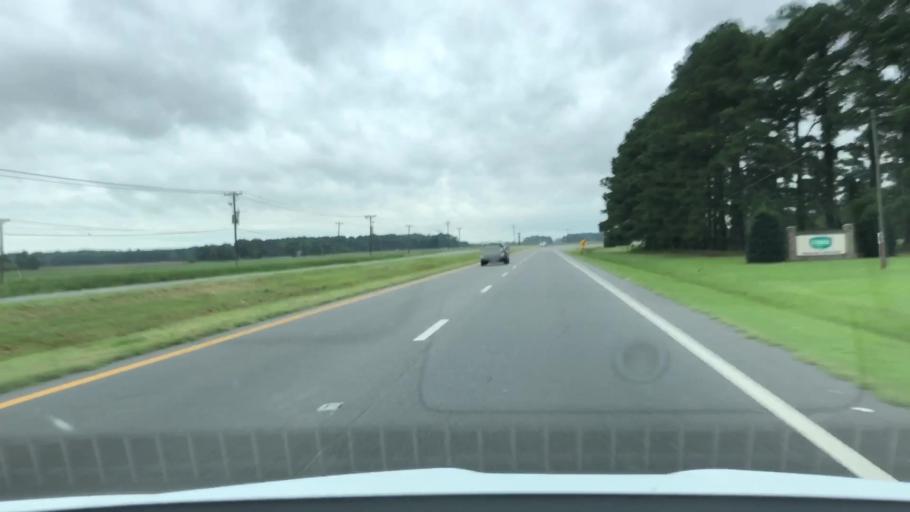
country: US
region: North Carolina
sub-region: Lenoir County
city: La Grange
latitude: 35.2602
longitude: -77.7095
